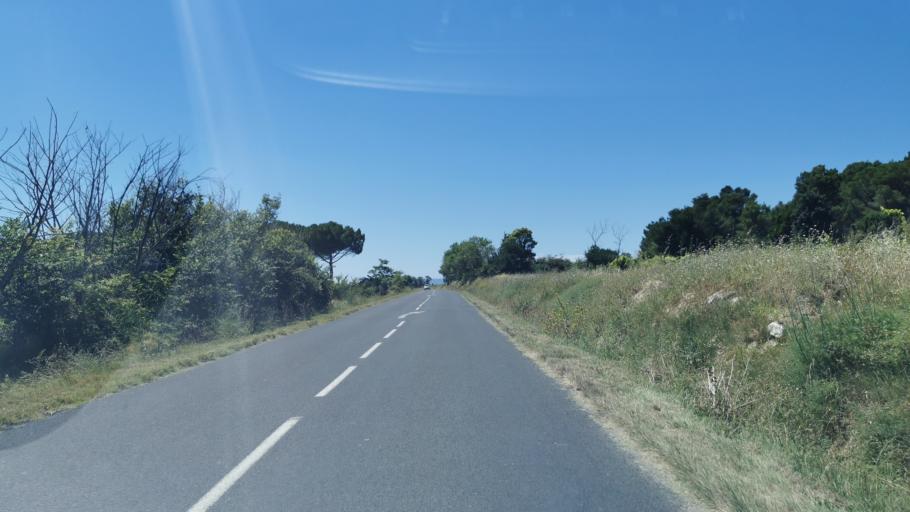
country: FR
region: Languedoc-Roussillon
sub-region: Departement de l'Aude
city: Vinassan
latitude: 43.2318
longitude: 3.0889
